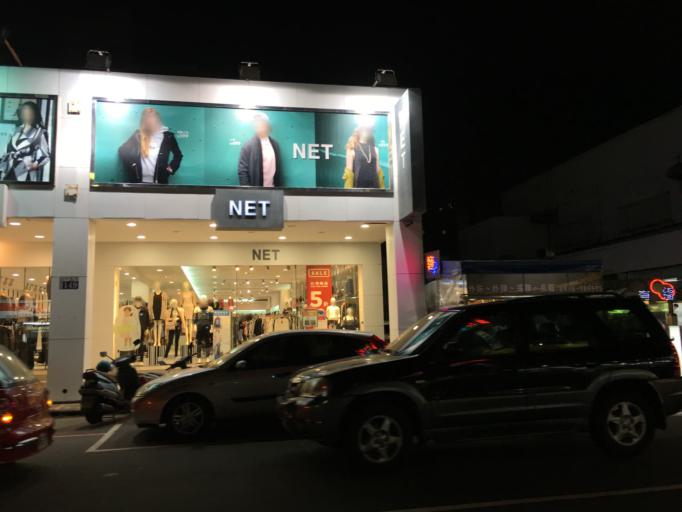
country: TW
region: Taiwan
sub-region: Taichung City
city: Taichung
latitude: 24.1854
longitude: 120.6214
